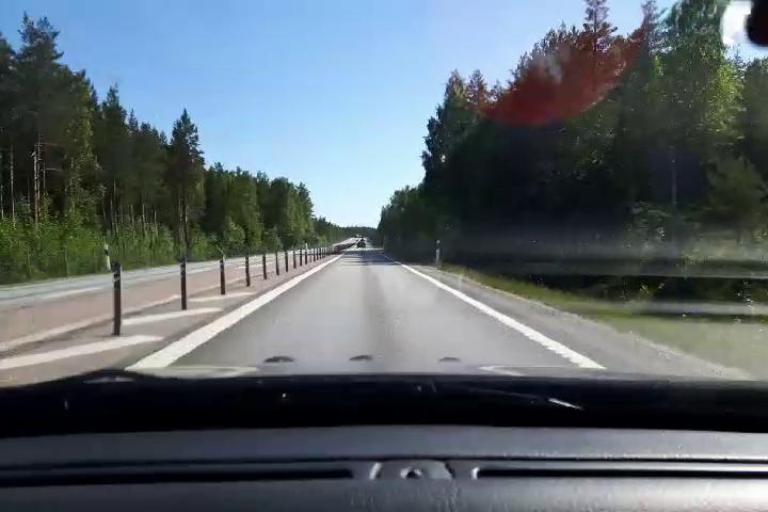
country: SE
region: Gaevleborg
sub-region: Soderhamns Kommun
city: Ljusne
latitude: 61.1226
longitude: 17.0144
